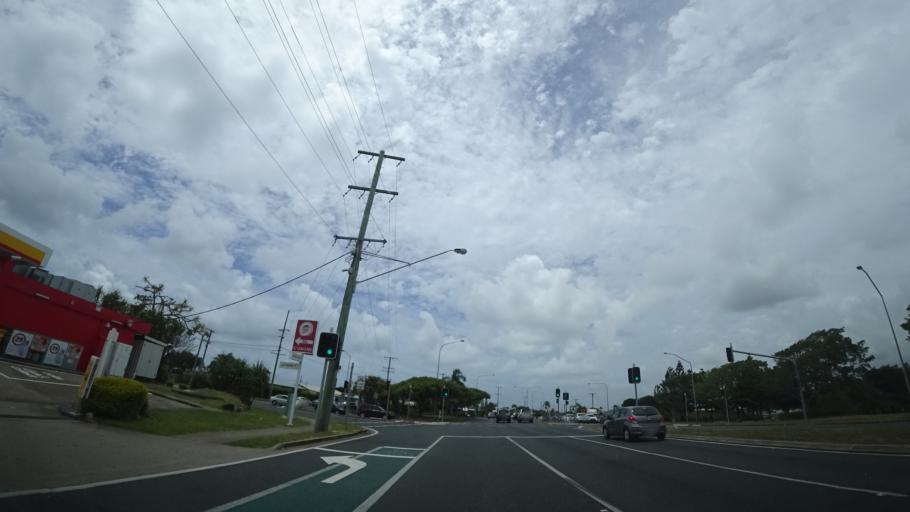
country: AU
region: Queensland
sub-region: Sunshine Coast
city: Mooloolaba
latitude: -26.7051
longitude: 153.1299
